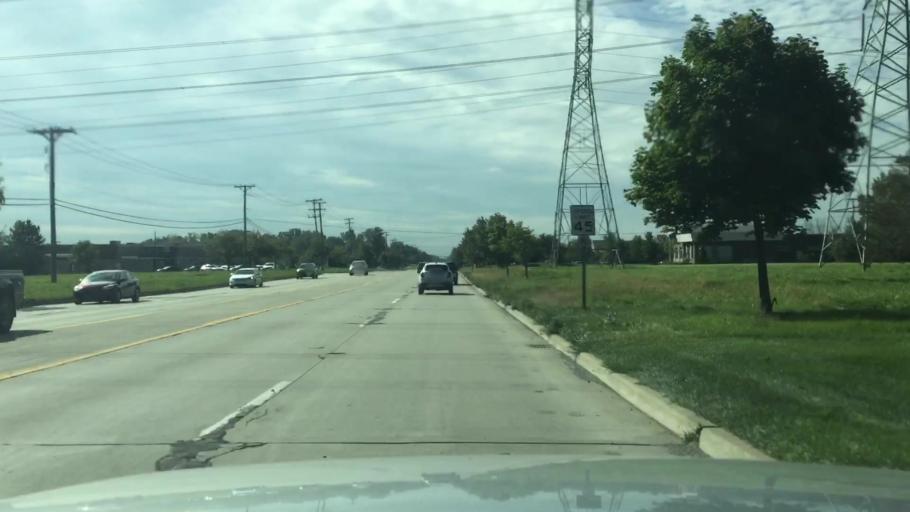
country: US
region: Michigan
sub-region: Wayne County
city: Canton
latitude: 42.3115
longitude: -83.4875
